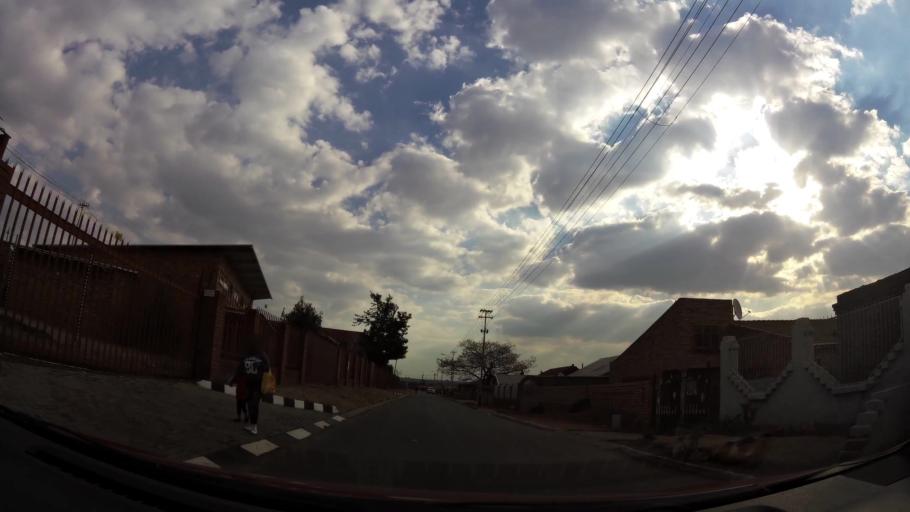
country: ZA
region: Gauteng
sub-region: City of Johannesburg Metropolitan Municipality
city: Soweto
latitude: -26.2252
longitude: 27.9341
